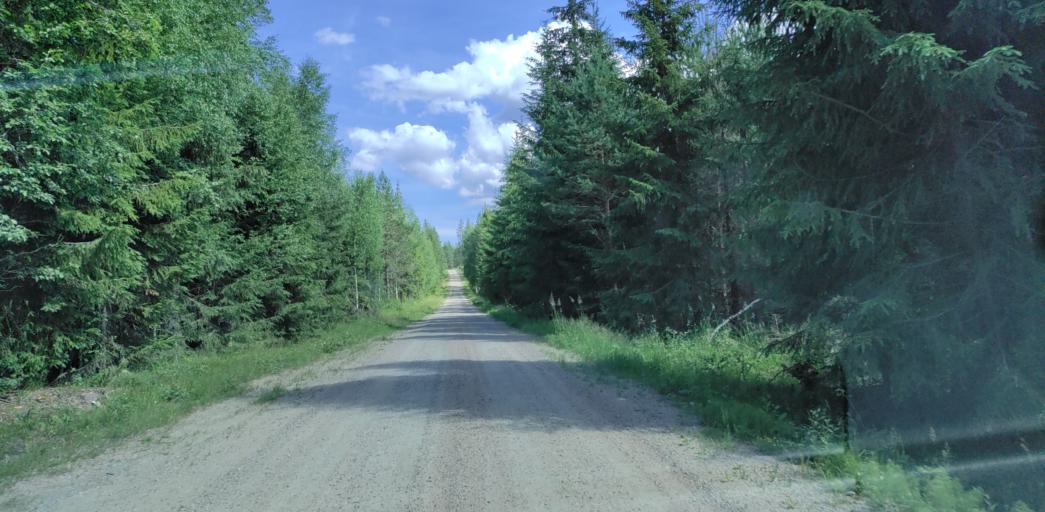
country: SE
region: Vaermland
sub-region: Hagfors Kommun
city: Ekshaerad
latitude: 60.0974
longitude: 13.4288
